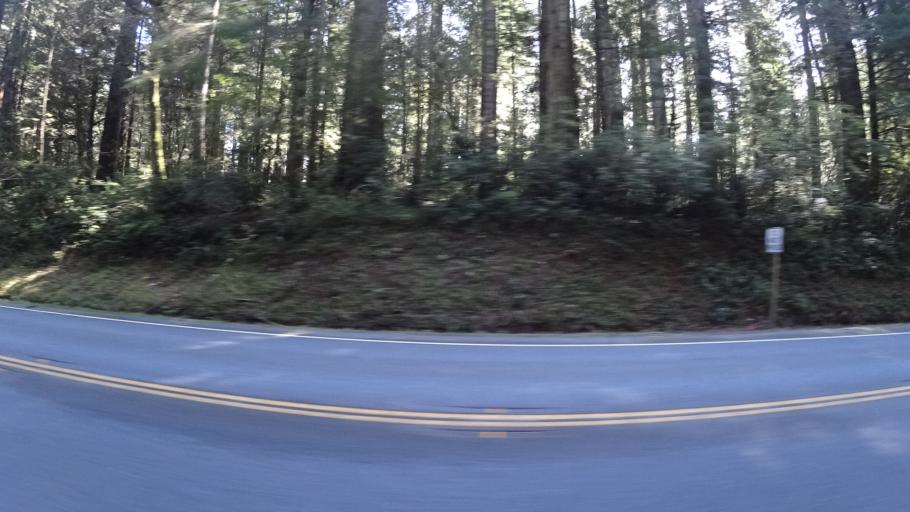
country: US
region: California
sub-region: Del Norte County
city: Bertsch-Oceanview
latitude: 41.6724
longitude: -124.1138
